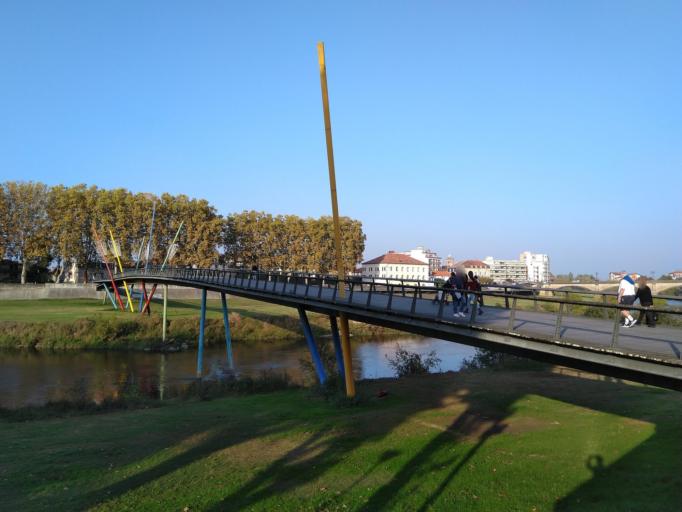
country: FR
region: Aquitaine
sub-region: Departement des Landes
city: Dax
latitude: 43.7114
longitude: -1.0576
